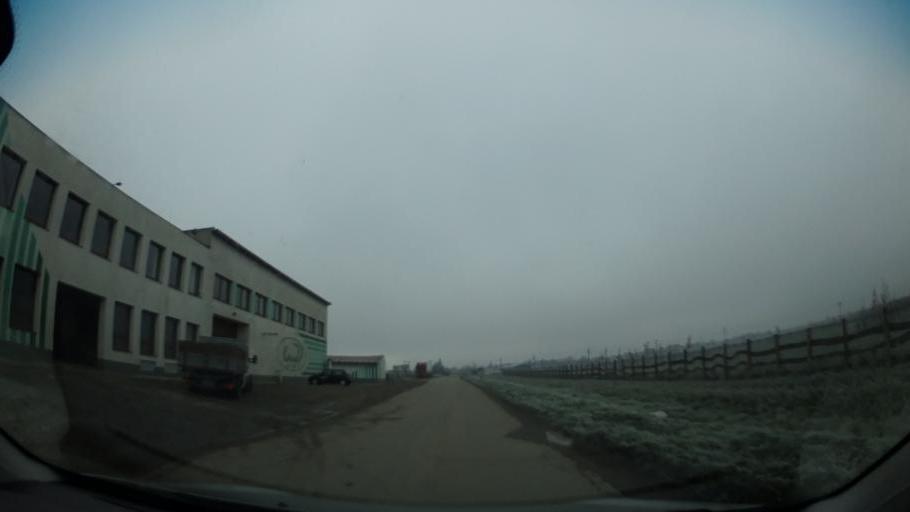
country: CZ
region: Vysocina
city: Mohelno
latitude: 49.1238
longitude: 16.1978
